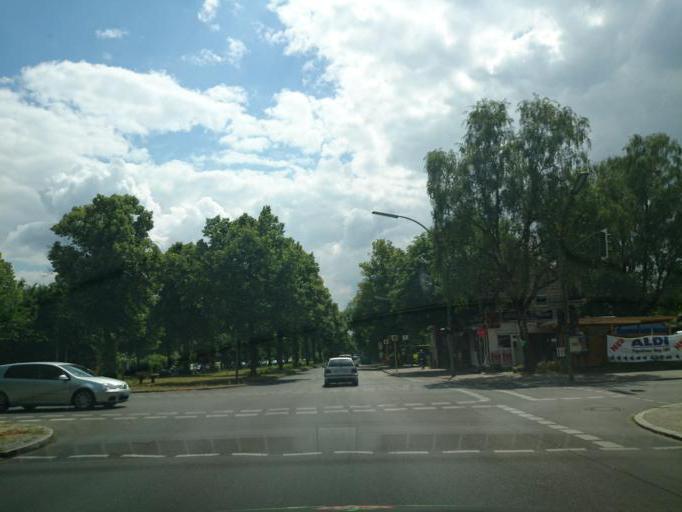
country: DE
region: Berlin
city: Lichtenrade
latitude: 52.3987
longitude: 13.4062
